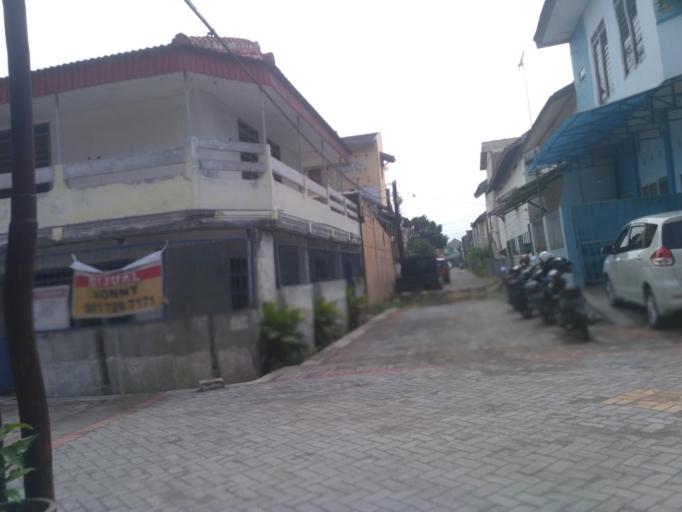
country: ID
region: Central Java
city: Semarang
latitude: -6.9575
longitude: 110.4041
